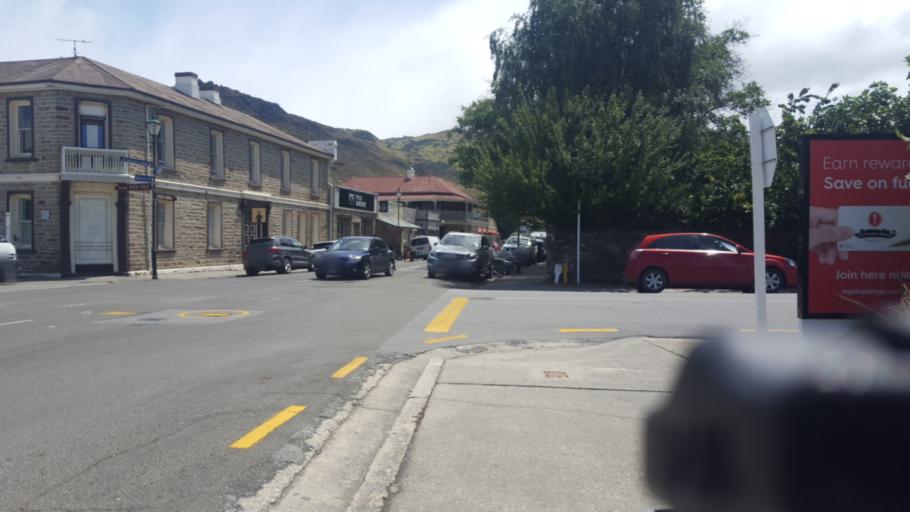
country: NZ
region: Otago
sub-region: Queenstown-Lakes District
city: Wanaka
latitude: -45.1871
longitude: 169.3169
